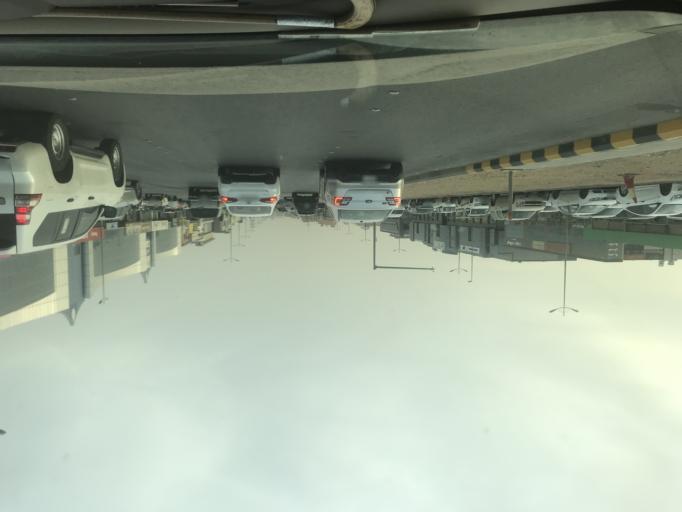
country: SA
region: Ar Riyad
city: Riyadh
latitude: 24.8008
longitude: 46.7400
